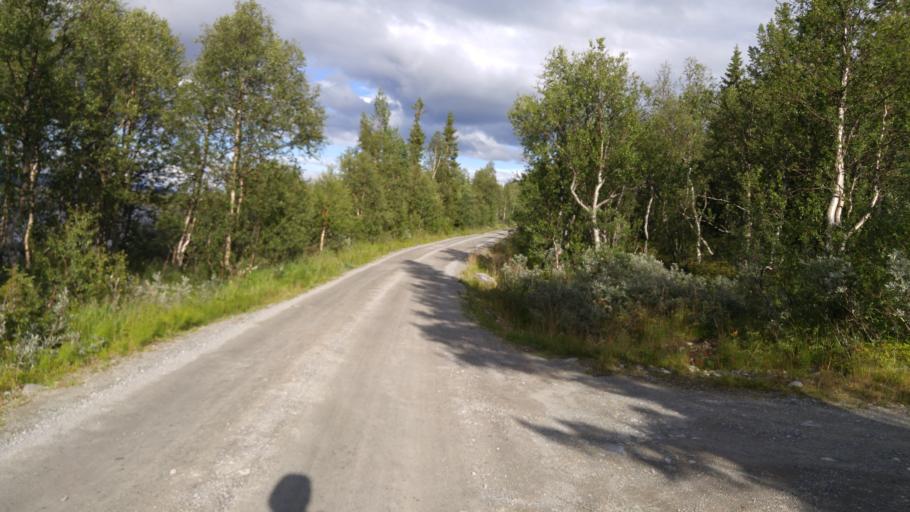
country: NO
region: Buskerud
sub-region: Hemsedal
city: Troim
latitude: 60.8513
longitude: 8.6998
